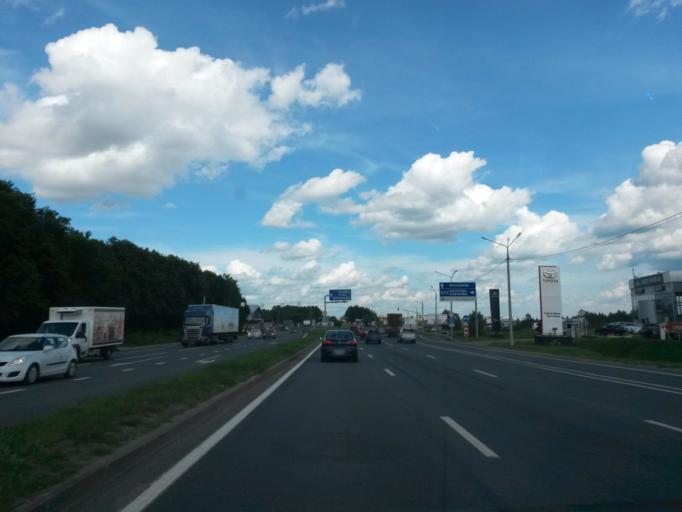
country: RU
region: Jaroslavl
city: Yaroslavl
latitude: 57.5620
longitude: 39.8254
